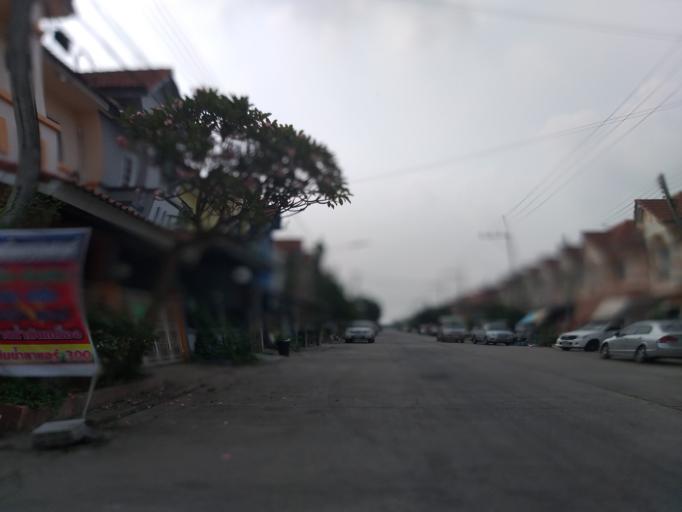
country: TH
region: Pathum Thani
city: Nong Suea
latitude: 14.0711
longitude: 100.8586
